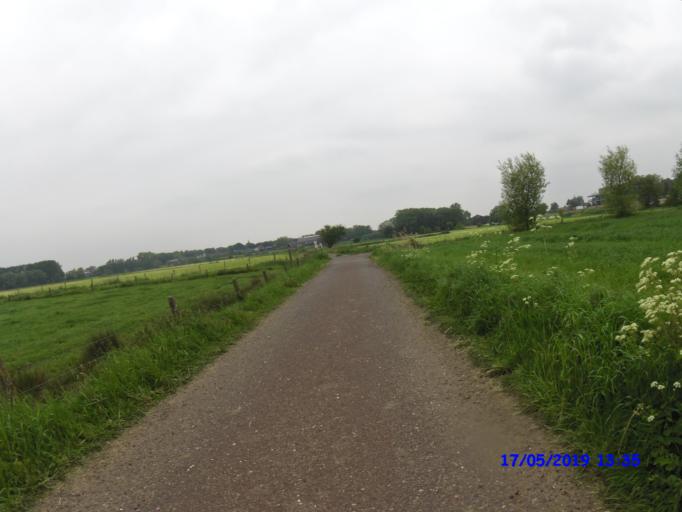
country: BE
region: Flanders
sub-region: Provincie West-Vlaanderen
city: Wielsbeke
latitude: 50.9072
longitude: 3.3912
